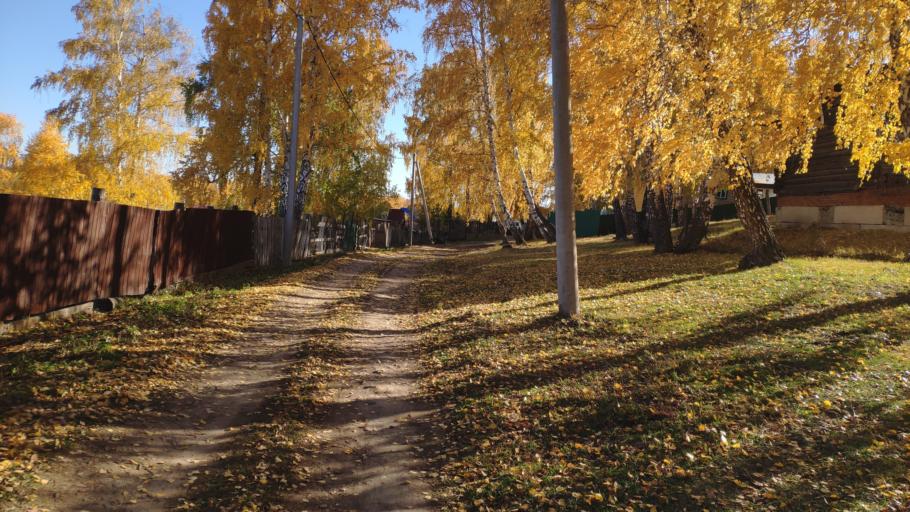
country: RU
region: Bashkortostan
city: Abzakovo
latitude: 53.3443
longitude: 58.5029
